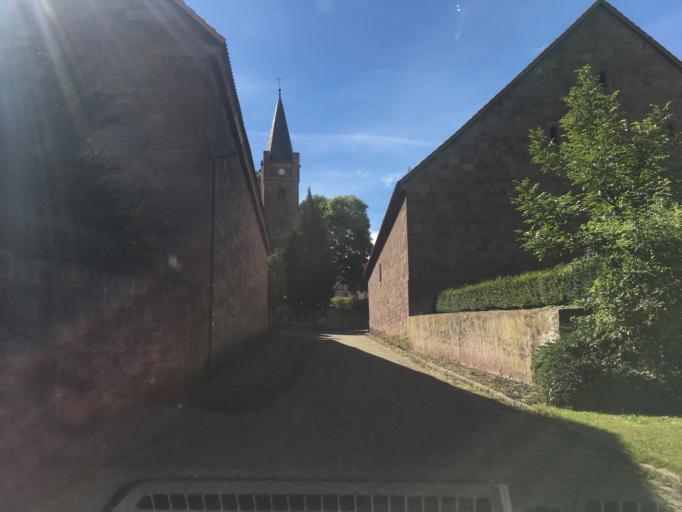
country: DE
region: Lower Saxony
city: Hameln
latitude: 52.0773
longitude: 9.3426
